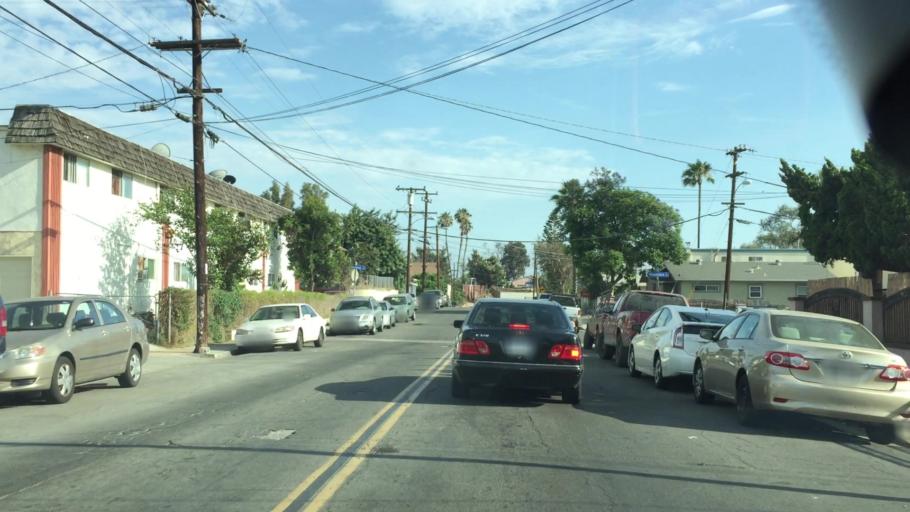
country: US
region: California
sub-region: San Diego County
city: Lemon Grove
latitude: 32.7480
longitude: -117.0837
